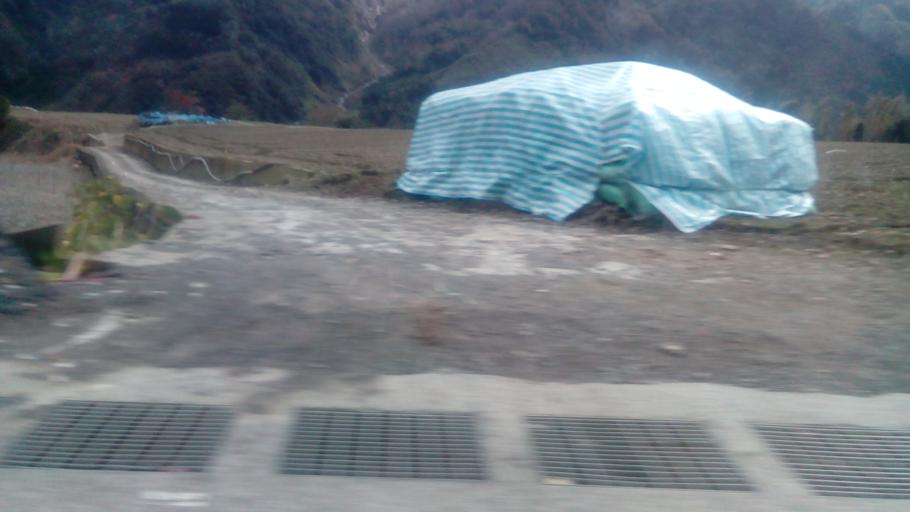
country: TW
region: Taiwan
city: Daxi
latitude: 24.4644
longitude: 121.3973
